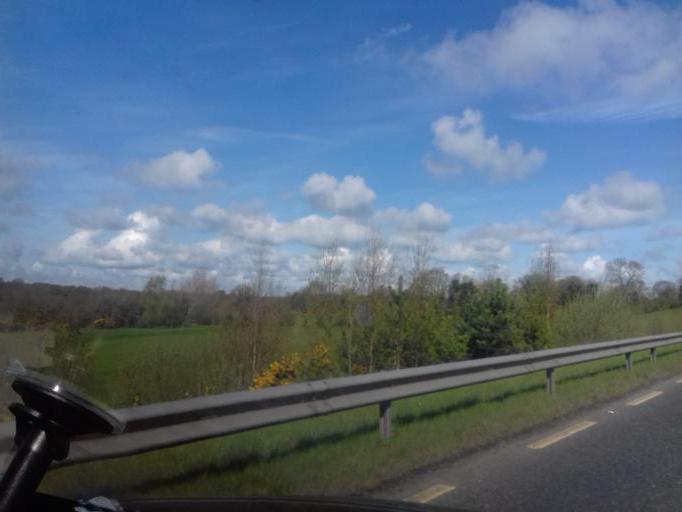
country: IE
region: Ulster
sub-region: An Cabhan
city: Mullagh
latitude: 53.7636
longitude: -6.9907
